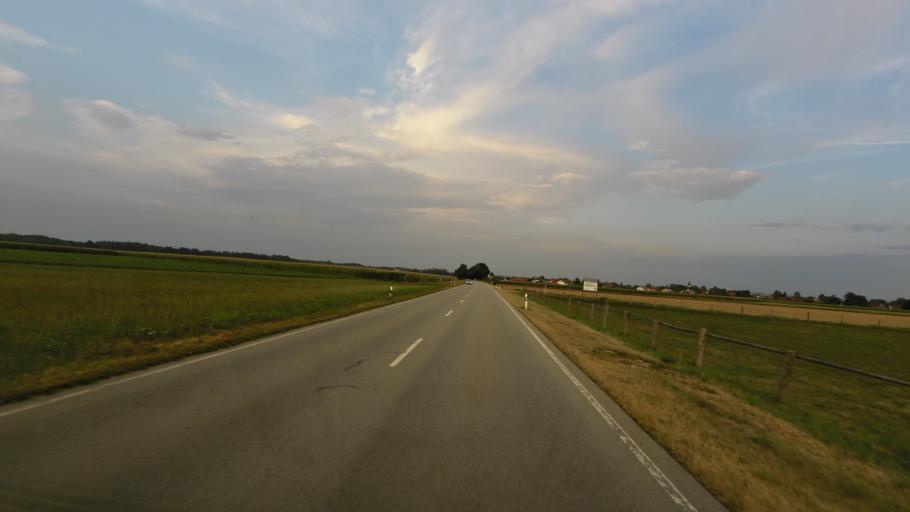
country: DE
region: Bavaria
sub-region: Lower Bavaria
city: Kirchham
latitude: 48.3512
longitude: 13.2545
